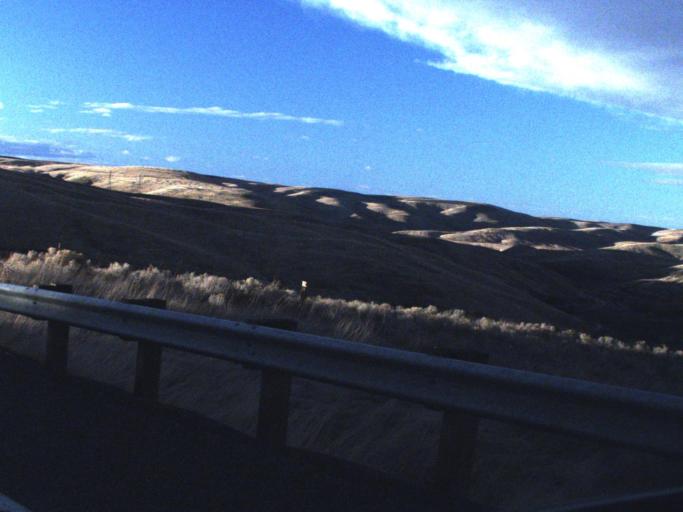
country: US
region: Washington
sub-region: Garfield County
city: Pomeroy
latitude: 46.5865
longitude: -117.7801
